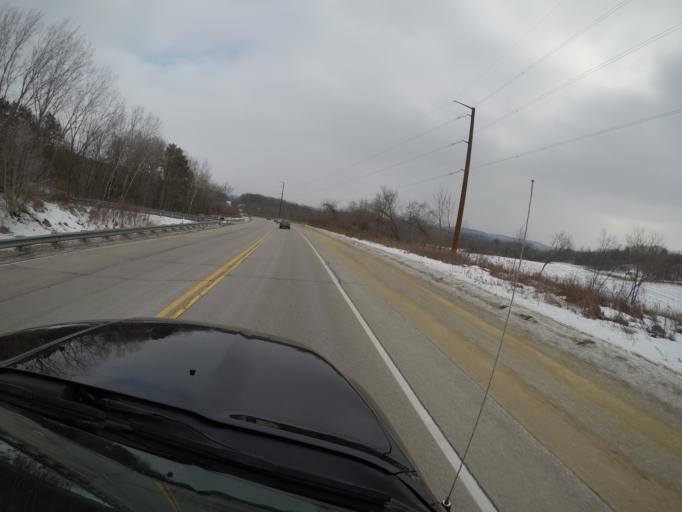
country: US
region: Wisconsin
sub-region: Trempealeau County
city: Galesville
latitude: 44.0710
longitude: -91.3205
